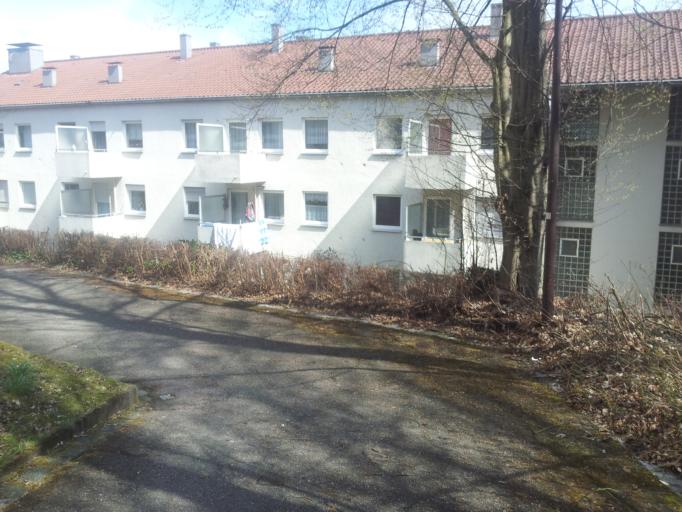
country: DE
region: Baden-Wuerttemberg
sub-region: Regierungsbezirk Stuttgart
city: Esslingen
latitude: 48.7440
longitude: 9.3258
